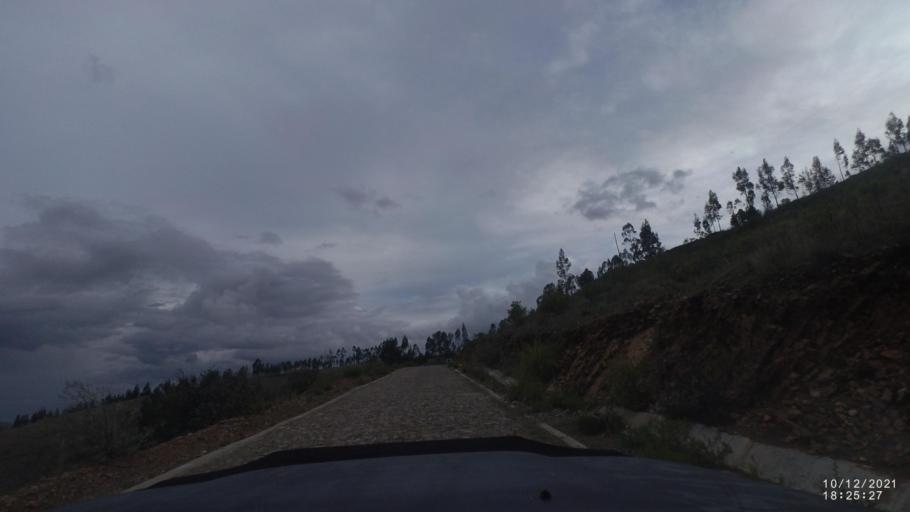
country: BO
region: Cochabamba
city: Tarata
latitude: -17.7922
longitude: -65.9729
